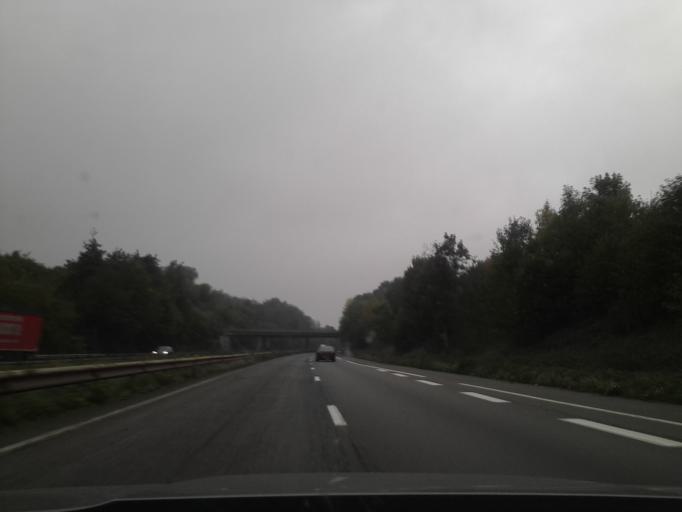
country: FR
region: Nord-Pas-de-Calais
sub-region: Departement du Nord
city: Saultain
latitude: 50.3426
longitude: 3.5687
